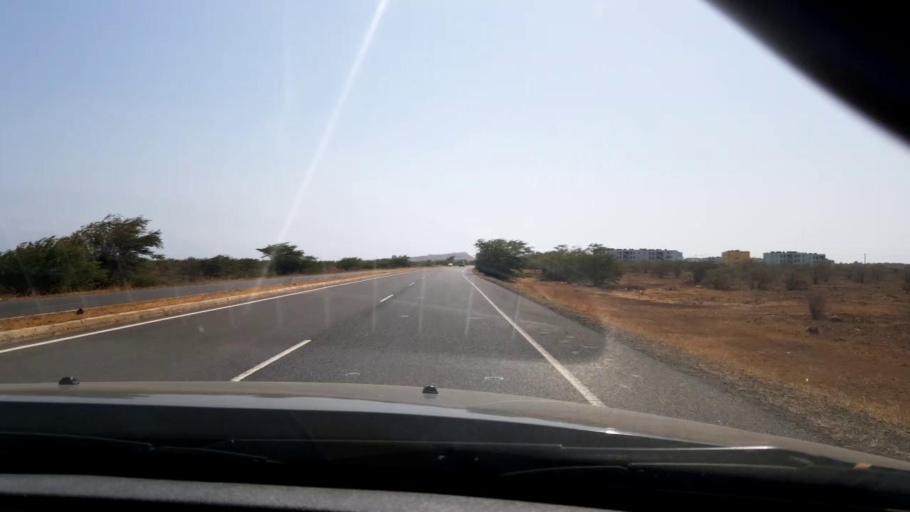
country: CV
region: Praia
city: Praia
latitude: 14.9561
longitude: -23.4947
